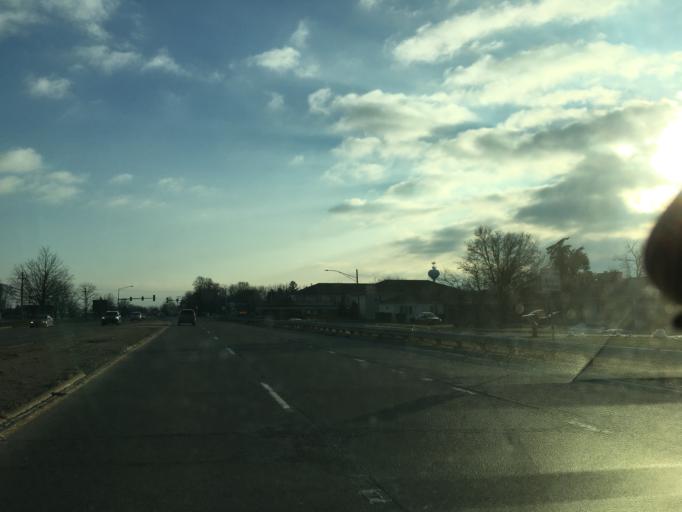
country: US
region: Illinois
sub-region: Kane County
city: Sugar Grove
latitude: 41.7639
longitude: -88.4426
